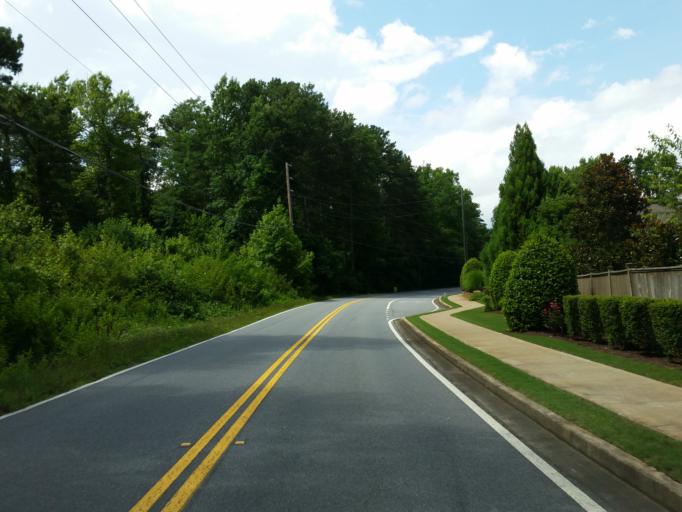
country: US
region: Georgia
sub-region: Fulton County
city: Roswell
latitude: 34.0541
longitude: -84.4360
